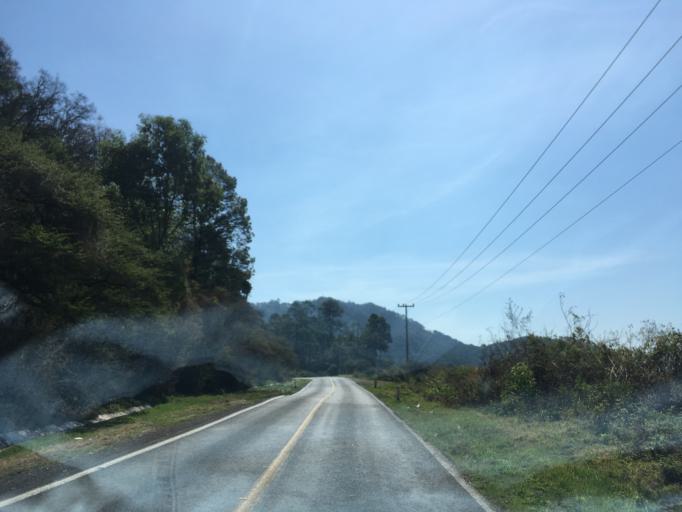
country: MX
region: Michoacan
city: Tzitzio
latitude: 19.6488
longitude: -100.9876
